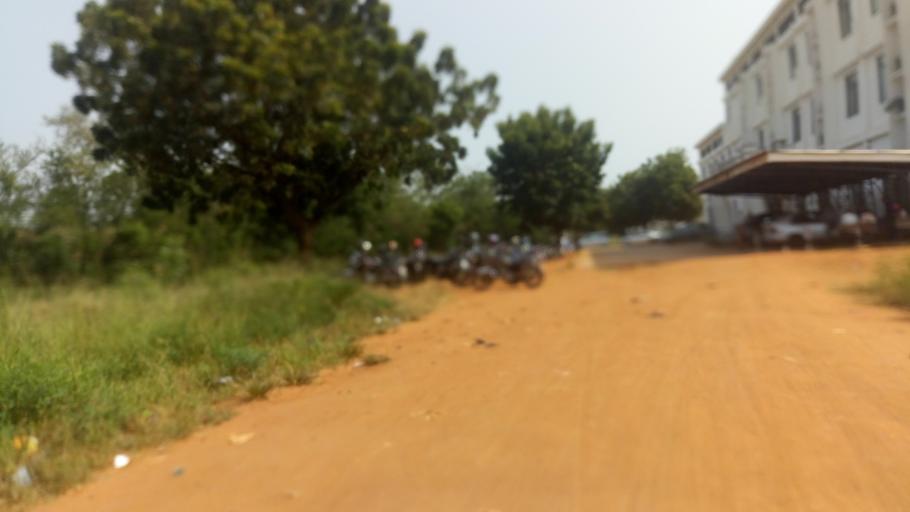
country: TG
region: Maritime
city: Lome
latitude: 6.1705
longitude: 1.2122
